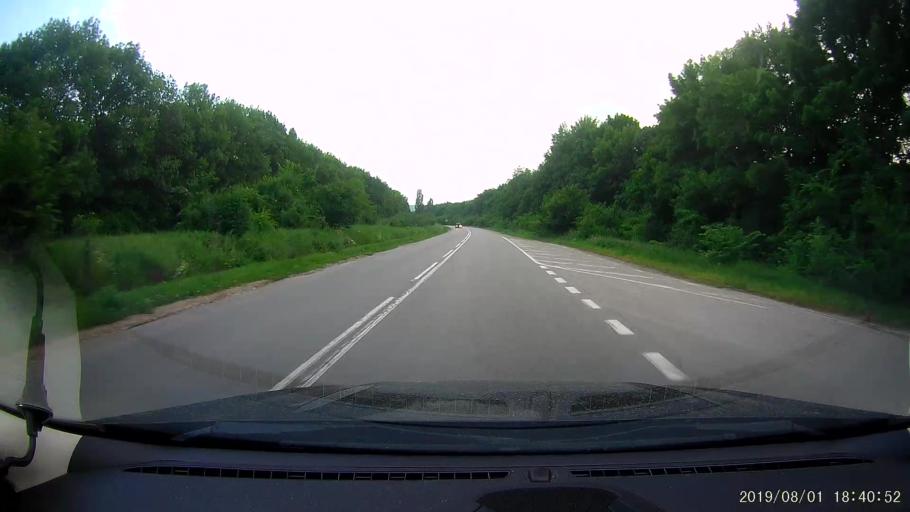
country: BG
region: Shumen
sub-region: Obshtina Khitrino
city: Gara Khitrino
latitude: 43.3569
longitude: 26.9213
